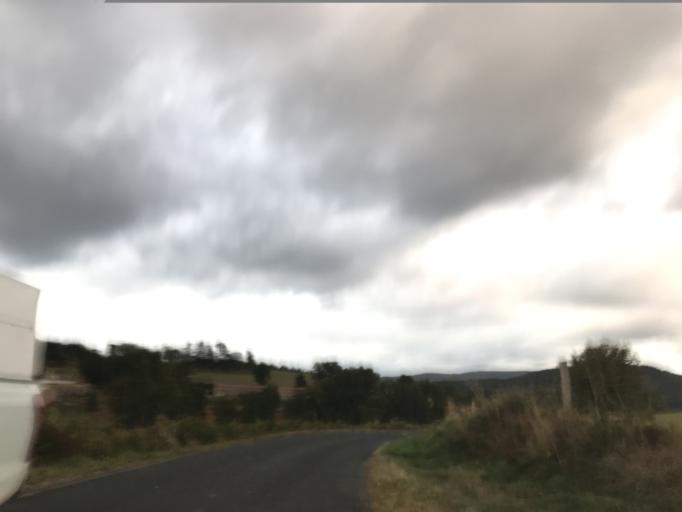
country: FR
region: Auvergne
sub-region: Departement du Puy-de-Dome
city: Celles-sur-Durolle
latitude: 45.8435
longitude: 3.6209
